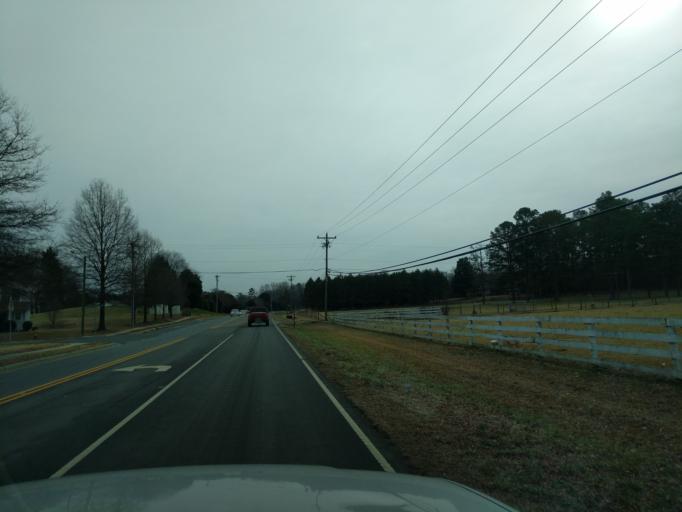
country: US
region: North Carolina
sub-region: Mecklenburg County
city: Huntersville
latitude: 35.3215
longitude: -80.8965
